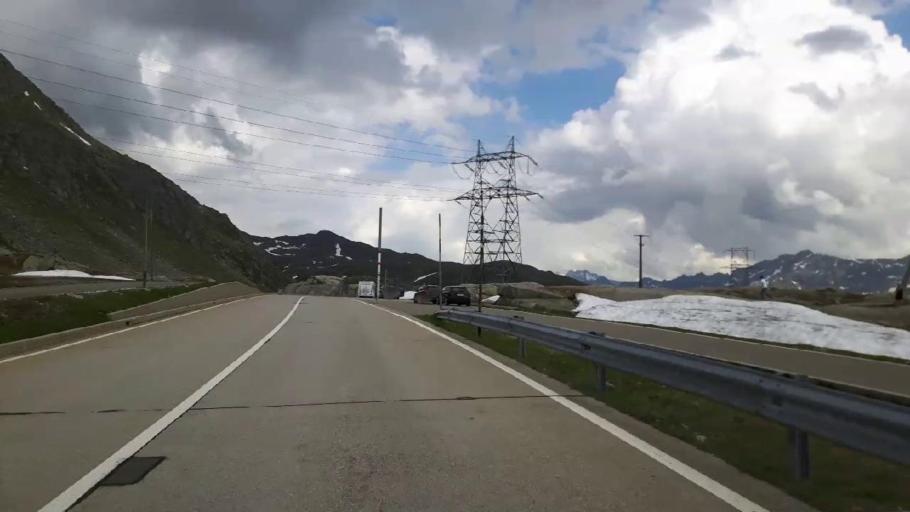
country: CH
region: Ticino
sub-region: Leventina District
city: Airolo
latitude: 46.5597
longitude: 8.5600
